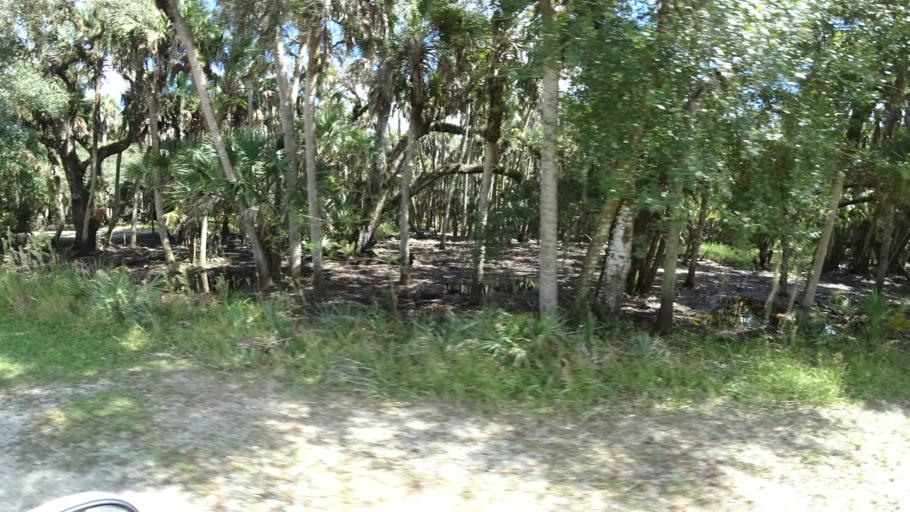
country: US
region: Florida
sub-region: Sarasota County
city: Lake Sarasota
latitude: 27.2754
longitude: -82.2664
